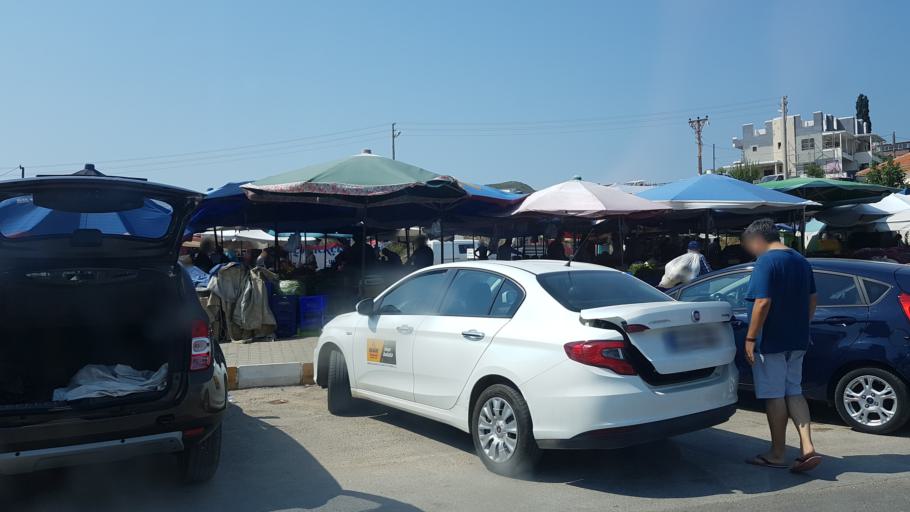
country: TR
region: Izmir
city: Urla
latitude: 38.3634
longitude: 26.7691
